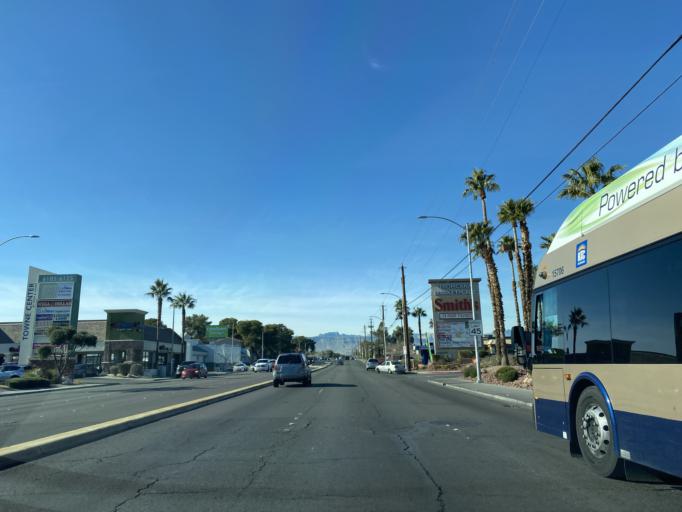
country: US
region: Nevada
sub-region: Clark County
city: Spring Valley
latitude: 36.1000
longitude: -115.2258
